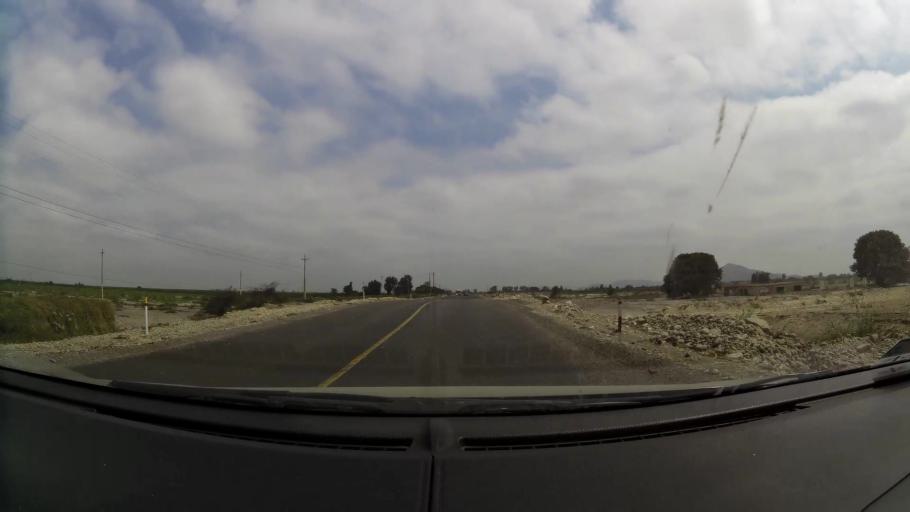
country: PE
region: La Libertad
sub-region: Ascope
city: Chicama
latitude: -7.8141
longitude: -79.1795
